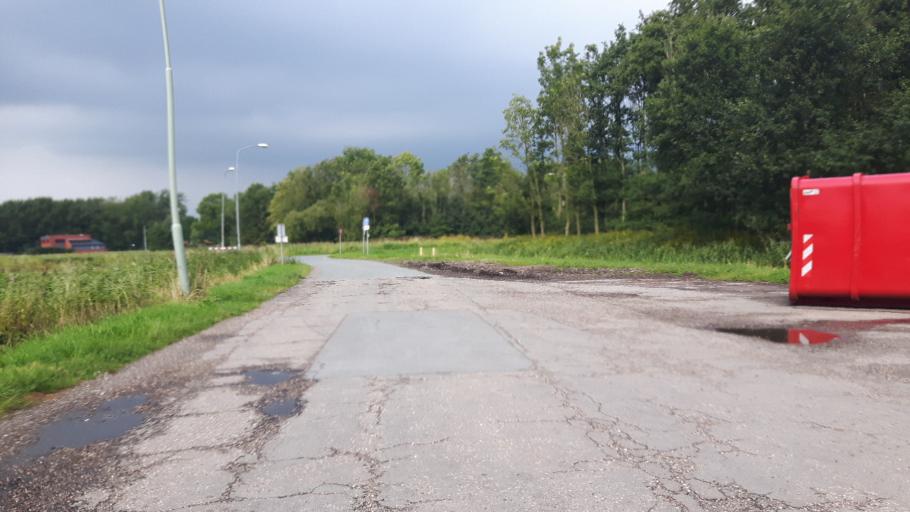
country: NL
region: Groningen
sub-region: Gemeente Bedum
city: Bedum
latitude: 53.3405
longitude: 6.6485
